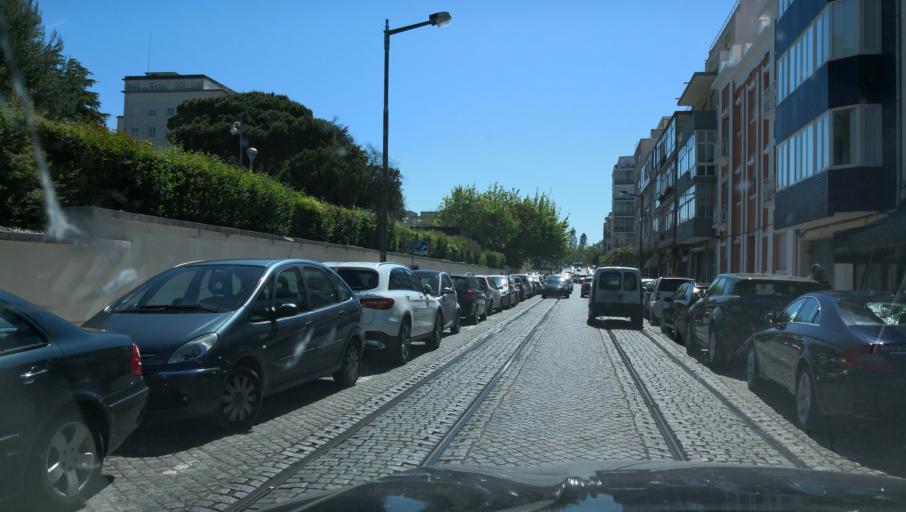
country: PT
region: Lisbon
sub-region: Lisbon
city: Lisbon
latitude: 38.7396
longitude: -9.1634
